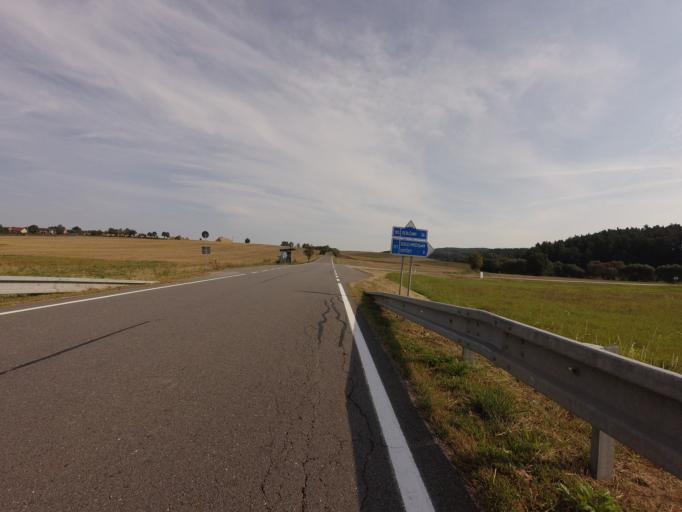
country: CZ
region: Jihocesky
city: Milevsko
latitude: 49.4755
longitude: 14.3649
